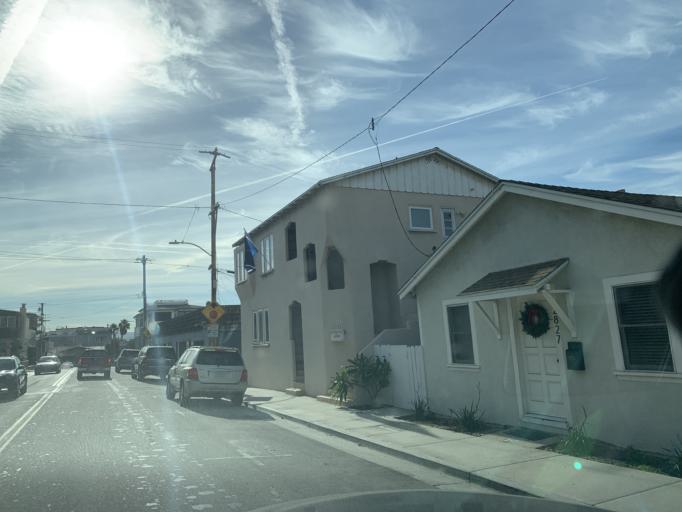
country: US
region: California
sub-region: Los Angeles County
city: Manhattan Beach
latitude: 33.8742
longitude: -118.4053
